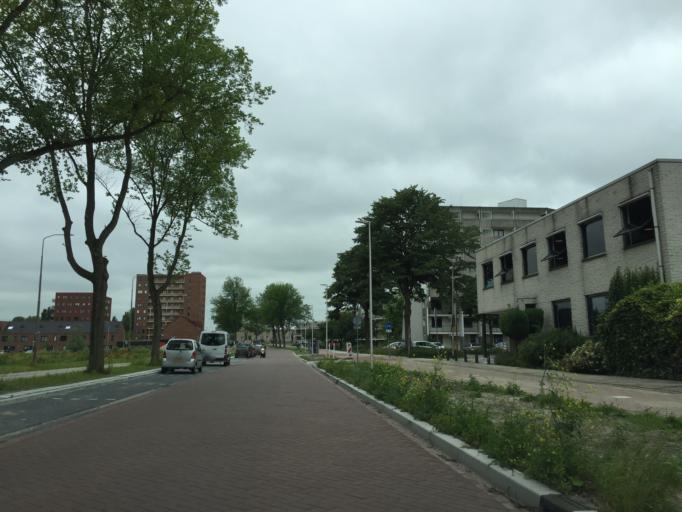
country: NL
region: South Holland
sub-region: Gemeente Zoetermeer
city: Zoetermeer
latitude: 52.0594
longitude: 4.5024
